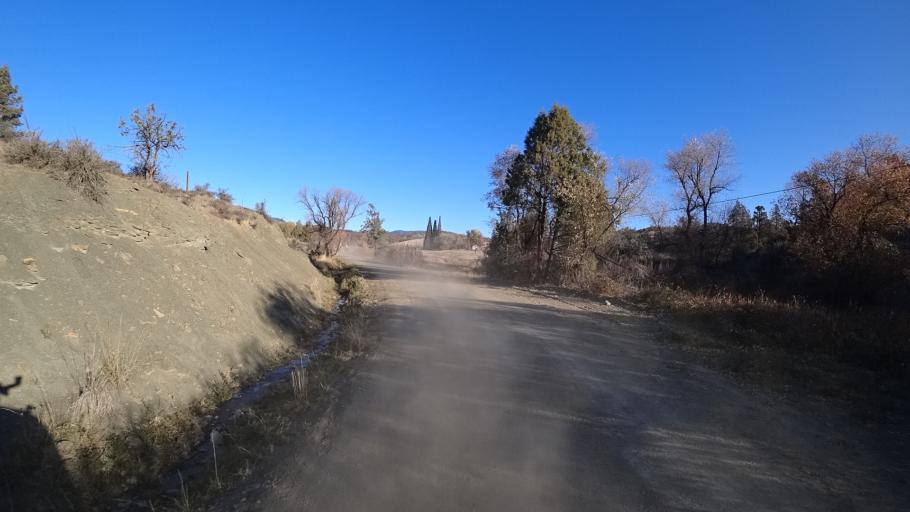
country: US
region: Oregon
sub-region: Jackson County
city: Ashland
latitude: 41.9915
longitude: -122.6234
